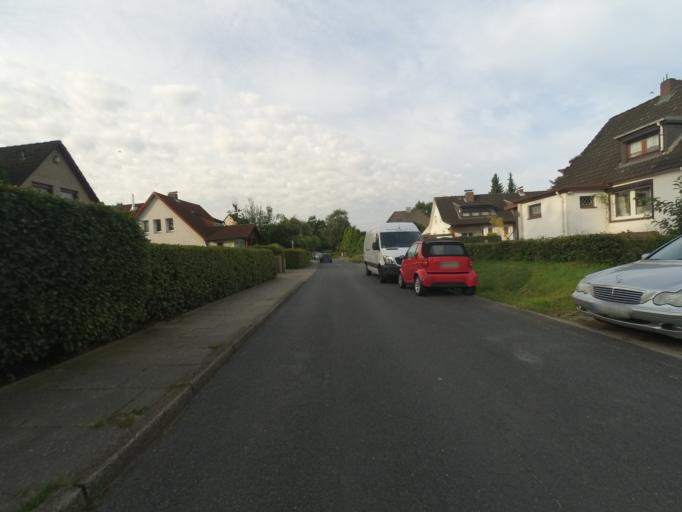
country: DE
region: Hamburg
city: Wandsbek
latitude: 53.5551
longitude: 10.1188
